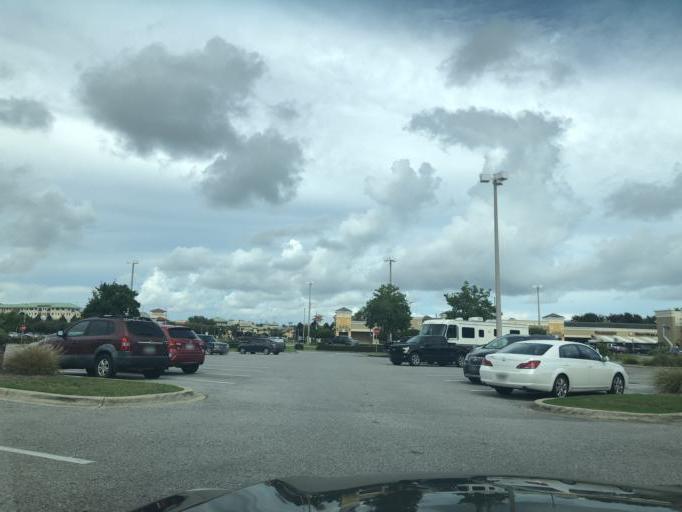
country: US
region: Florida
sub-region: Okaloosa County
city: Destin
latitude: 30.3905
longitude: -86.4292
